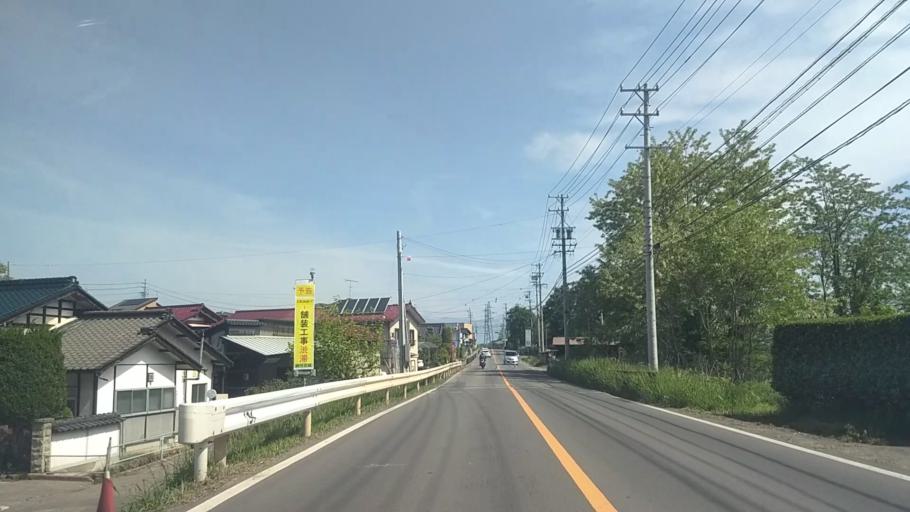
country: JP
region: Nagano
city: Saku
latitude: 36.1816
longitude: 138.4817
